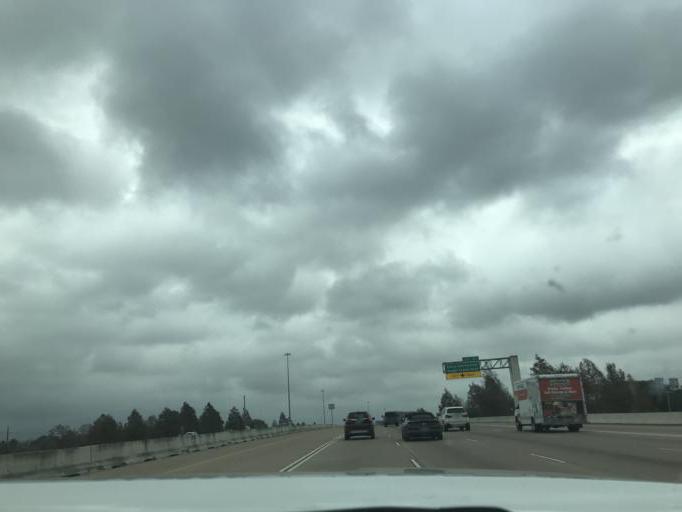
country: US
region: Texas
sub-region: Fort Bend County
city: Sugar Land
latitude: 29.6050
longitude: -95.6151
